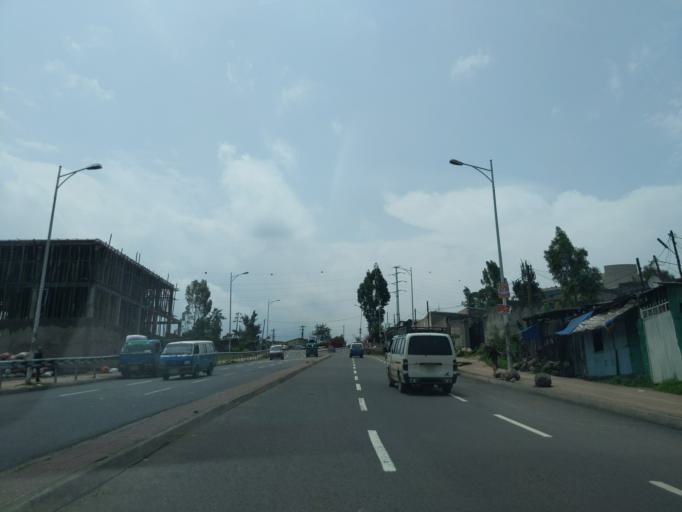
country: ET
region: Adis Abeba
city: Addis Ababa
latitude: 8.9507
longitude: 38.7593
